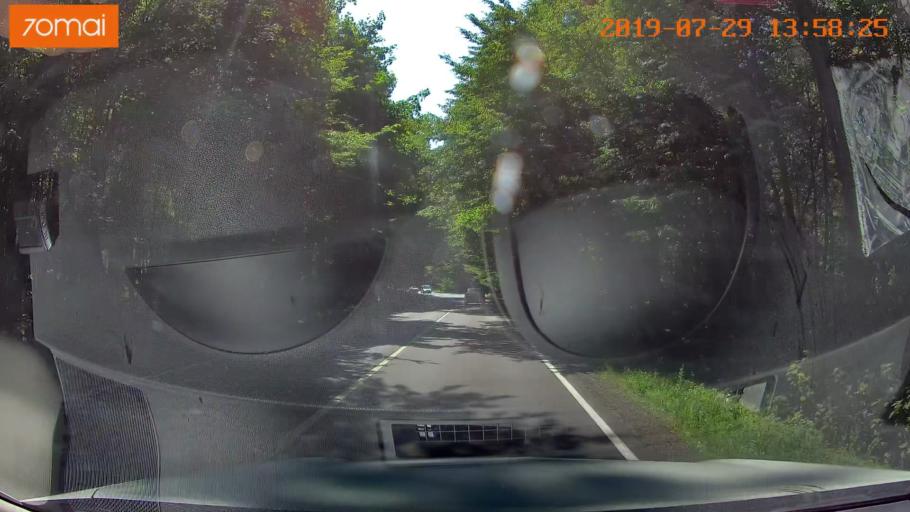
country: RU
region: Kaliningrad
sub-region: Gorod Kaliningrad
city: Baltiysk
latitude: 54.6938
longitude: 19.9369
